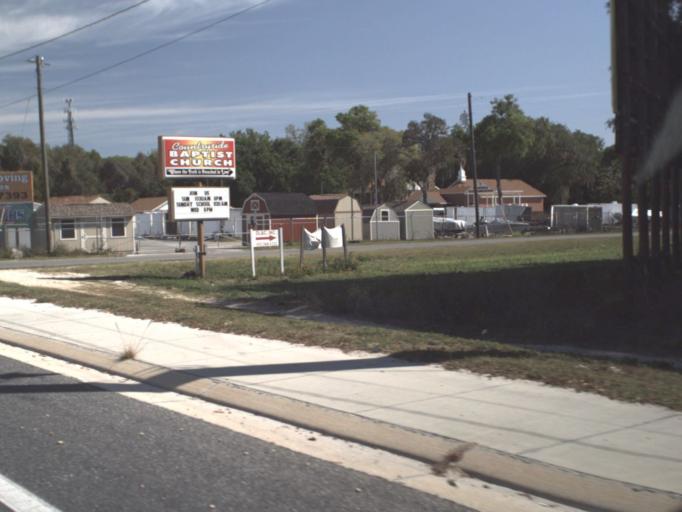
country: US
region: Florida
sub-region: Lake County
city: Fruitland Park
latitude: 28.8713
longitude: -81.9064
